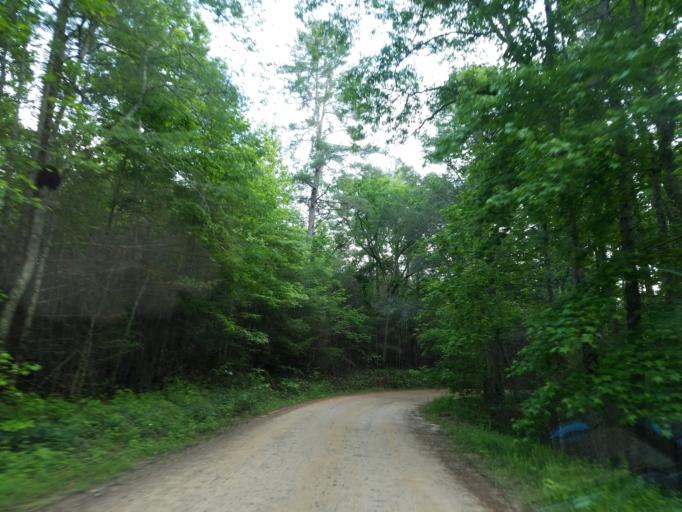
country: US
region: Georgia
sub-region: Lumpkin County
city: Dahlonega
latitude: 34.5789
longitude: -84.1246
